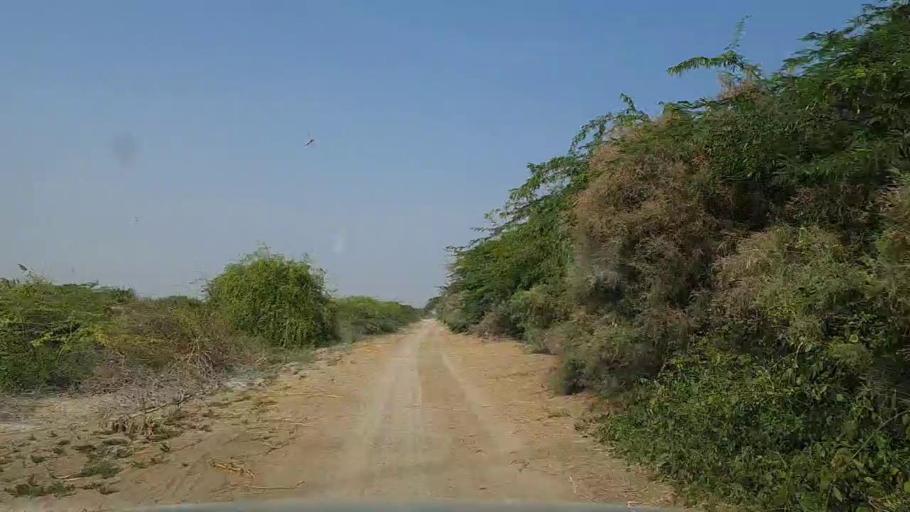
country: PK
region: Sindh
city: Mirpur Sakro
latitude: 24.5515
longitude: 67.5566
